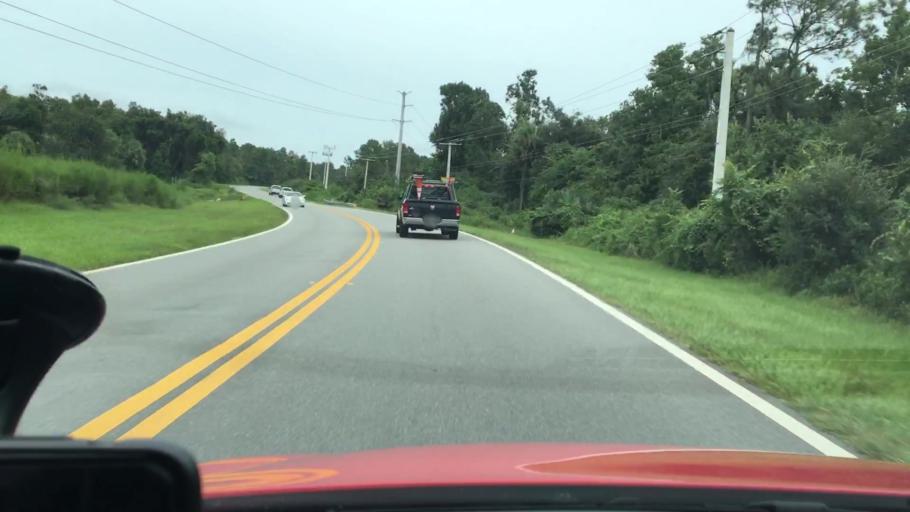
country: US
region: Florida
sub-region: Flagler County
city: Palm Coast
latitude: 29.5428
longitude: -81.2106
